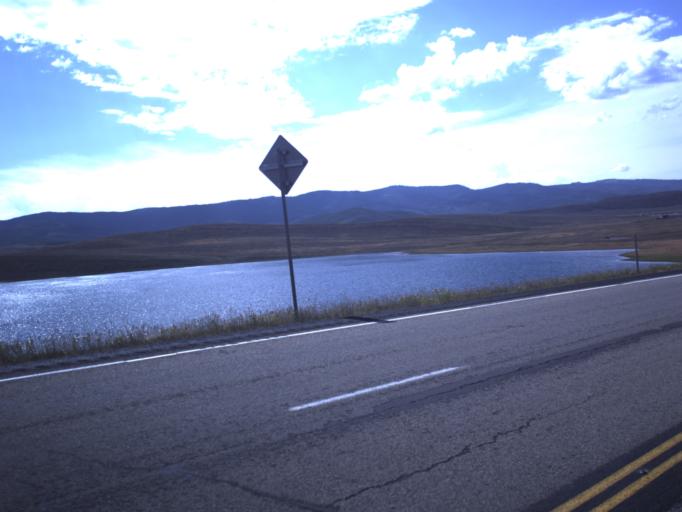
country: US
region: Utah
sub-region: Wasatch County
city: Heber
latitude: 40.2324
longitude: -111.1315
